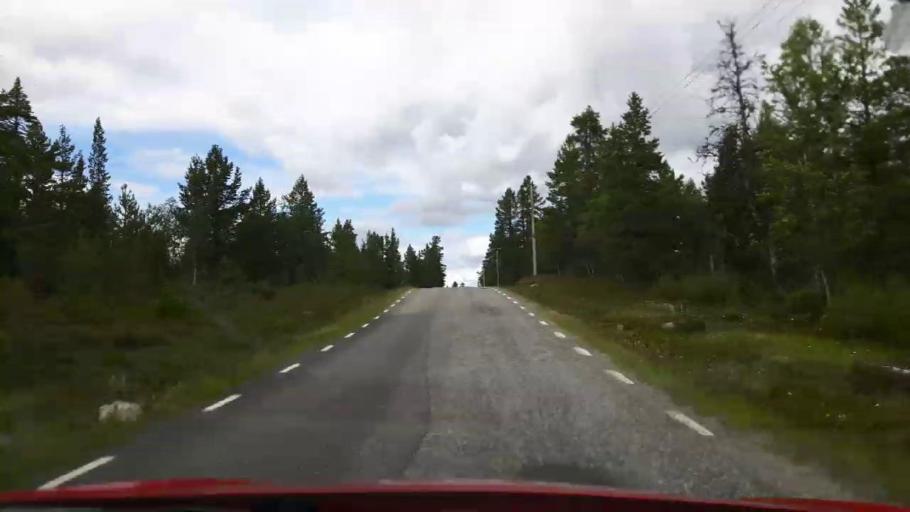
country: NO
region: Hedmark
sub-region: Engerdal
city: Engerdal
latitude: 62.3132
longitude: 12.8100
